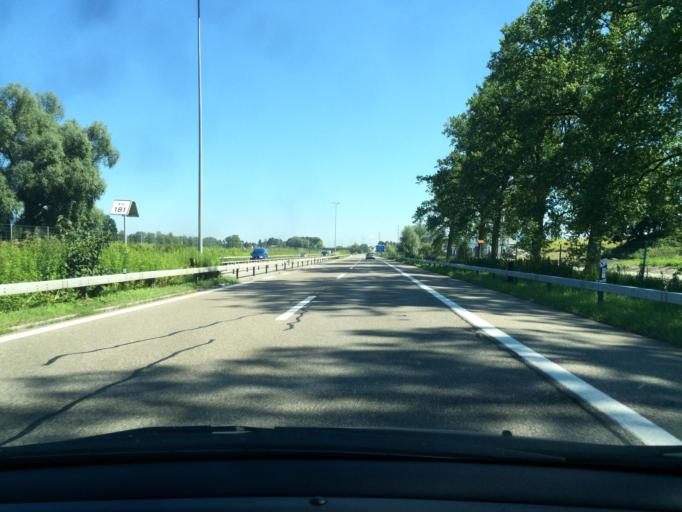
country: CH
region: Saint Gallen
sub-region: Wahlkreis Rheintal
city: Diepoldsau
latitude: 47.3849
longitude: 9.6403
